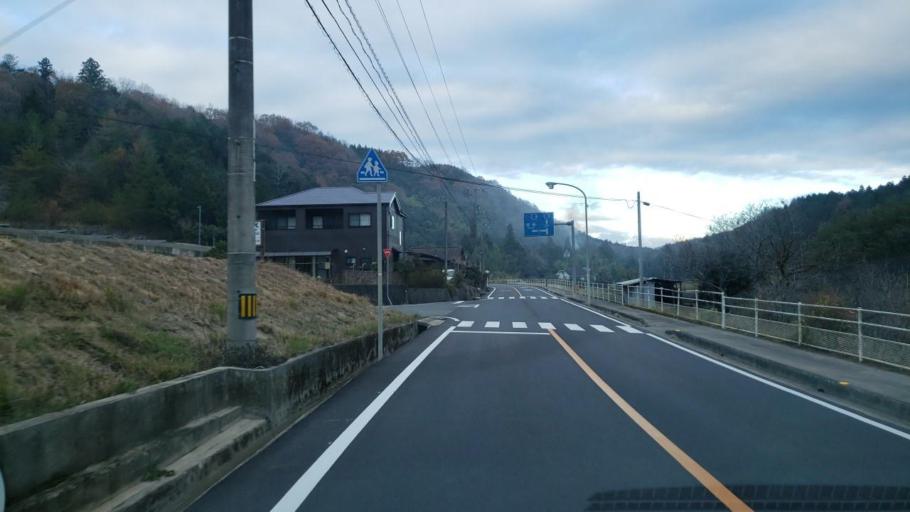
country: JP
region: Tokushima
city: Wakimachi
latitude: 34.1808
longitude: 134.1666
